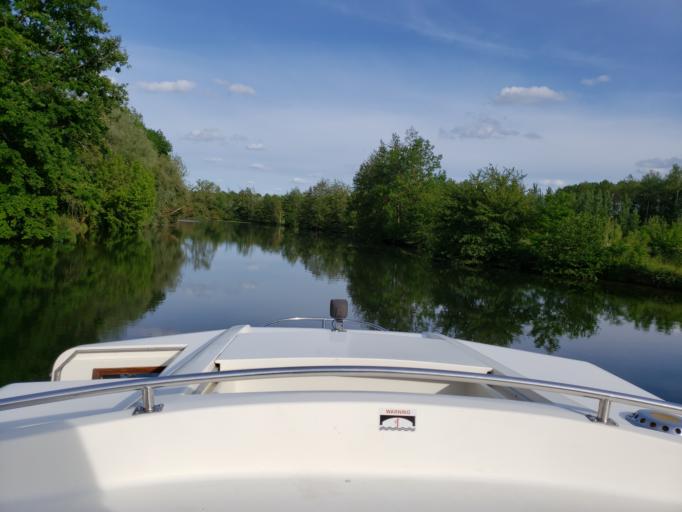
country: FR
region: Bourgogne
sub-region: Departement de l'Yonne
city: Migennes
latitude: 47.9427
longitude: 3.5073
